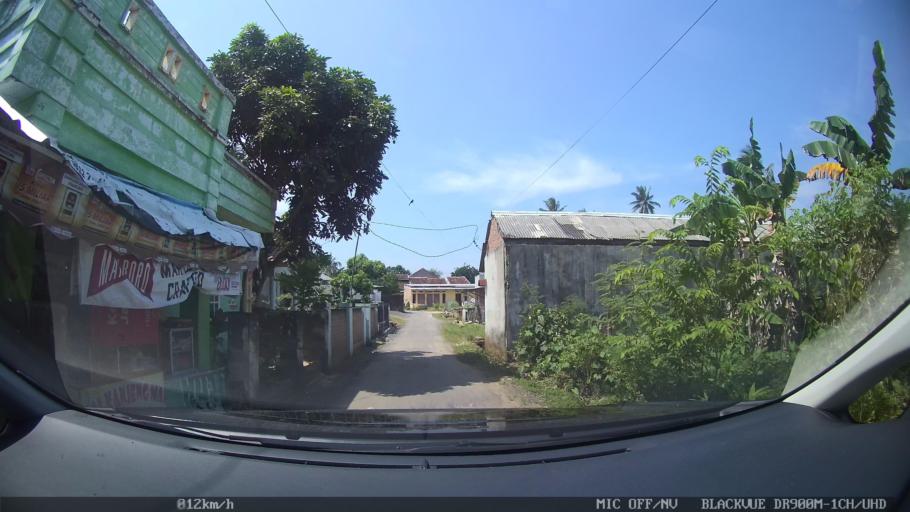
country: ID
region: Lampung
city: Kedaton
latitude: -5.3619
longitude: 105.2546
